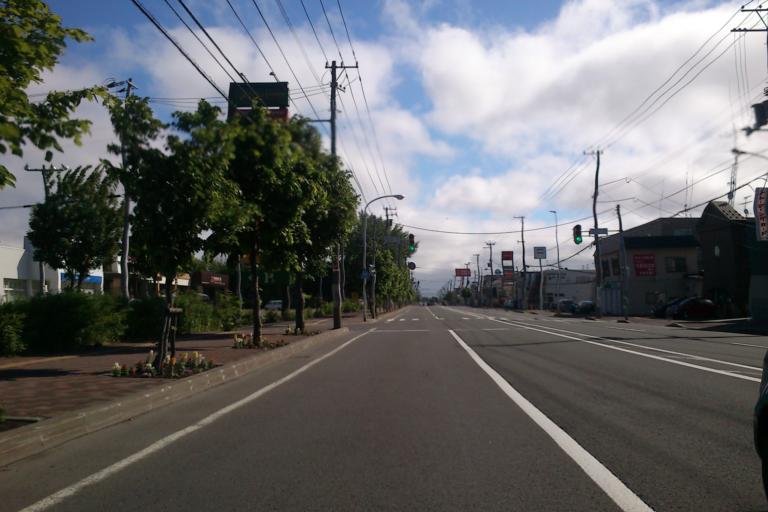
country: JP
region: Hokkaido
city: Sapporo
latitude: 43.1274
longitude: 141.2557
